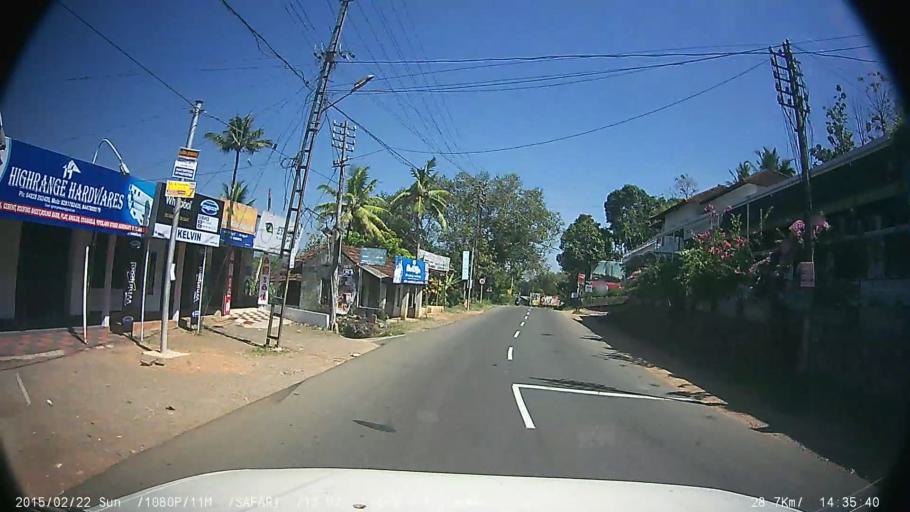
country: IN
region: Kerala
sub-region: Kottayam
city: Erattupetta
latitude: 9.5570
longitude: 76.7832
